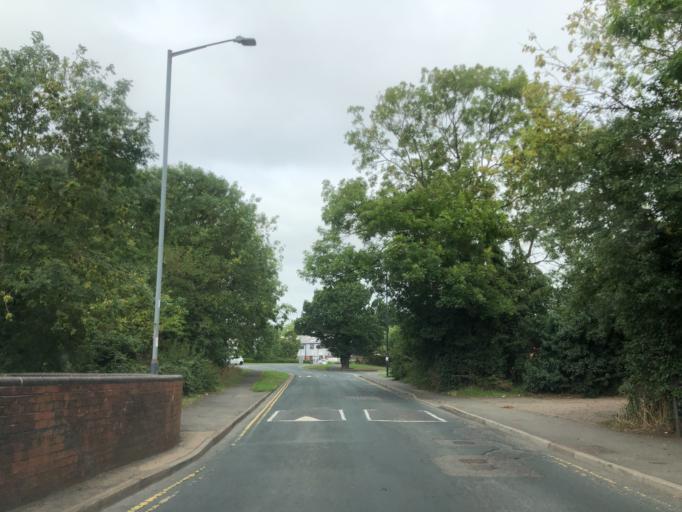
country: GB
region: England
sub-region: Warwickshire
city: Warwick
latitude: 52.2913
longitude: -1.5982
